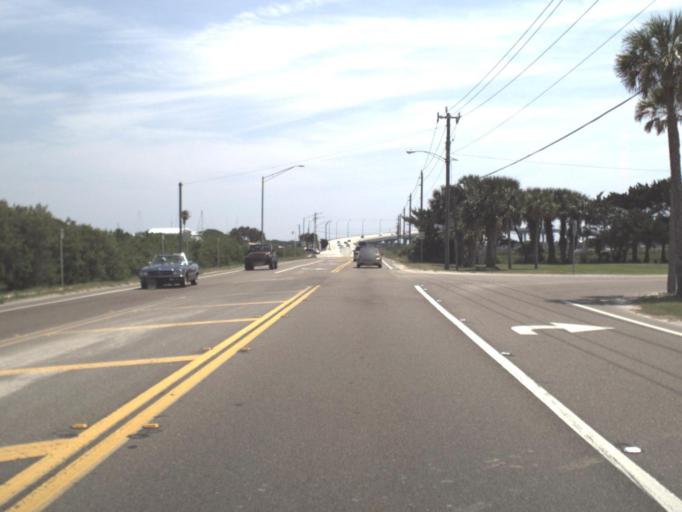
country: US
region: Florida
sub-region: Saint Johns County
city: Saint Augustine
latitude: 29.9127
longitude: -81.3100
